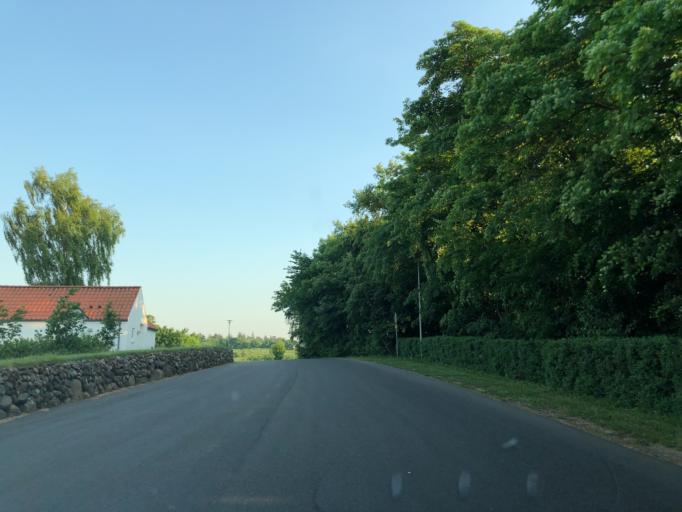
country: DK
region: Central Jutland
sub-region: Struer Kommune
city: Struer
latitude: 56.4345
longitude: 8.5056
